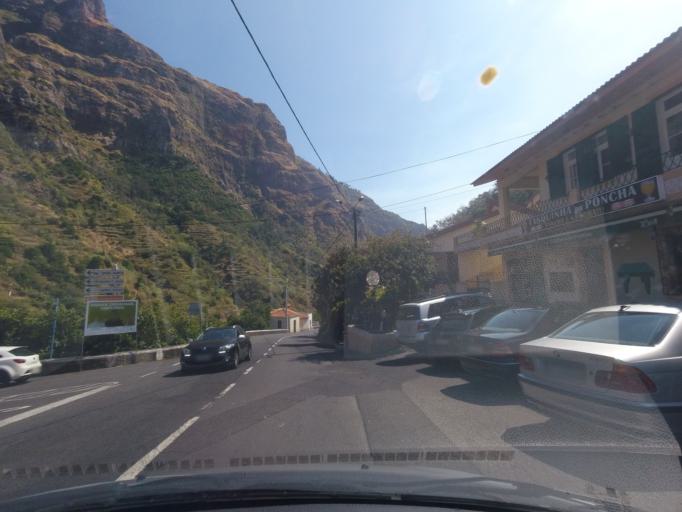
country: PT
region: Madeira
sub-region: Camara de Lobos
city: Curral das Freiras
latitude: 32.7266
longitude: -17.0284
